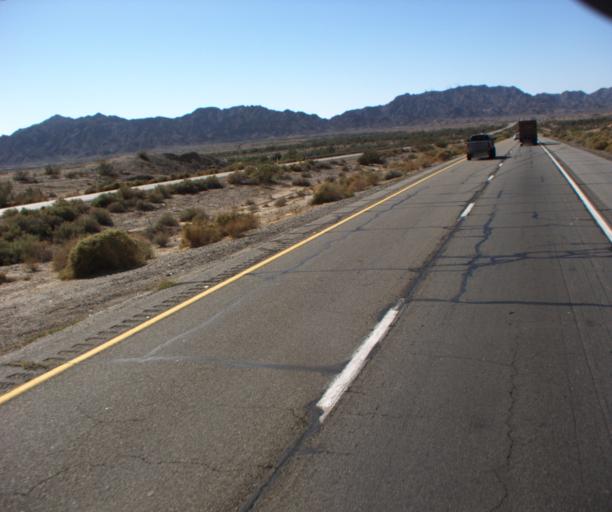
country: US
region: Arizona
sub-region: Yuma County
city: Wellton
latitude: 32.6619
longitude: -114.2620
